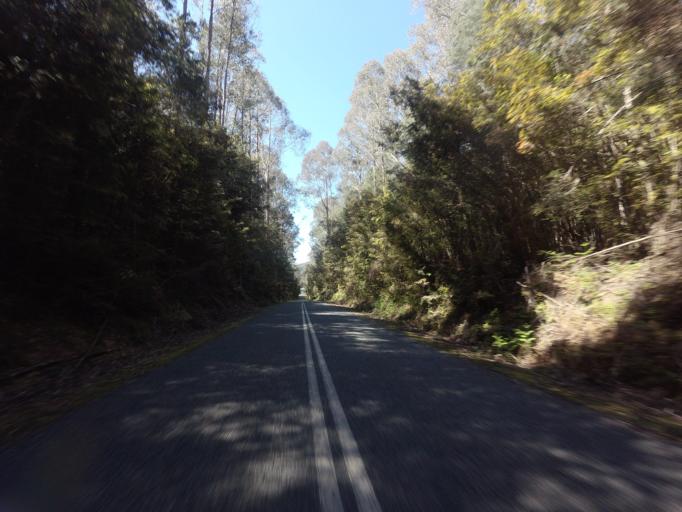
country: AU
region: Tasmania
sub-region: Derwent Valley
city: New Norfolk
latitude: -42.7451
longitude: 146.4149
